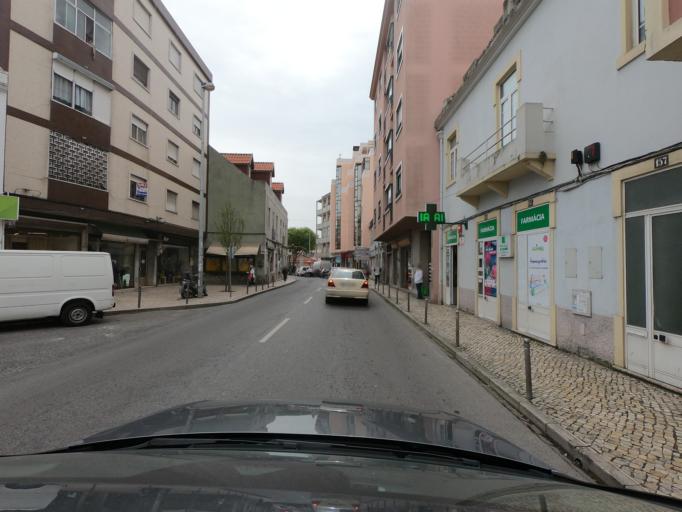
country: PT
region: Lisbon
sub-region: Sintra
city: Queluz
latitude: 38.7564
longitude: -9.2558
